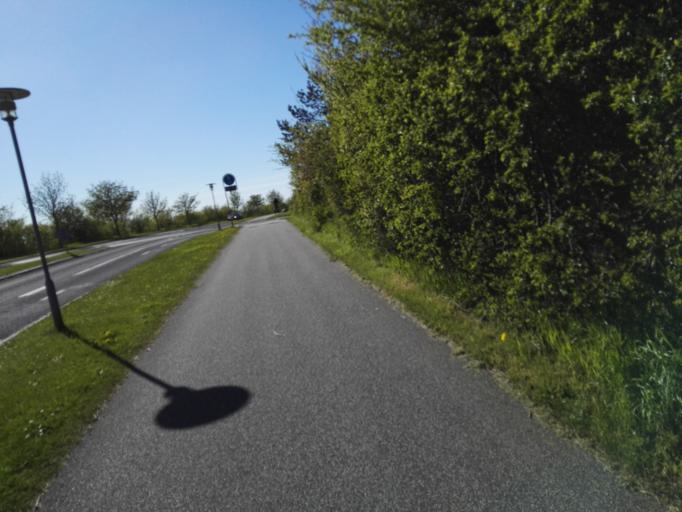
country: DK
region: Capital Region
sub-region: Egedal Kommune
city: Vekso
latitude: 55.7509
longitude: 12.2355
